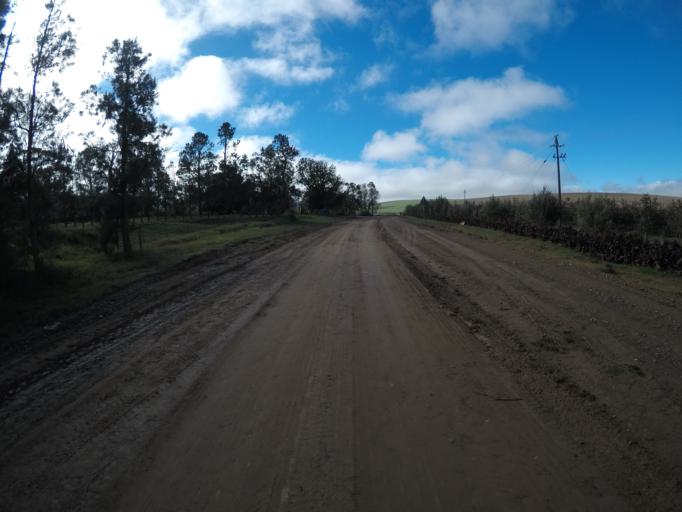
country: ZA
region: Western Cape
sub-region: Overberg District Municipality
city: Caledon
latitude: -34.1106
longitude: 19.7485
